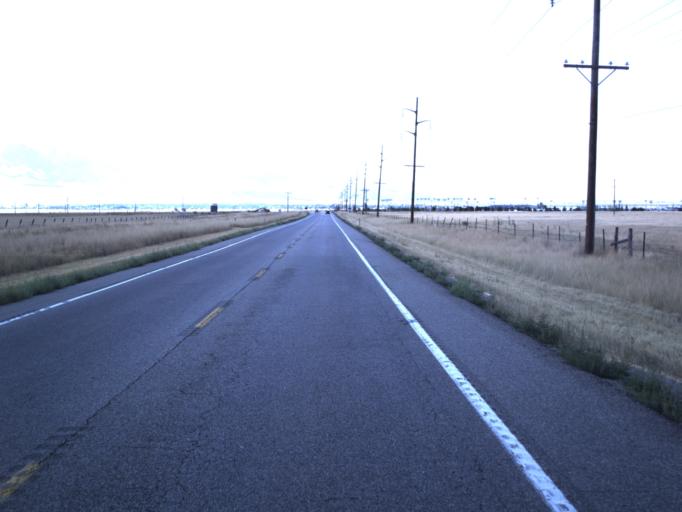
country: US
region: Utah
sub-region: Tooele County
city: Tooele
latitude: 40.5630
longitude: -112.3586
